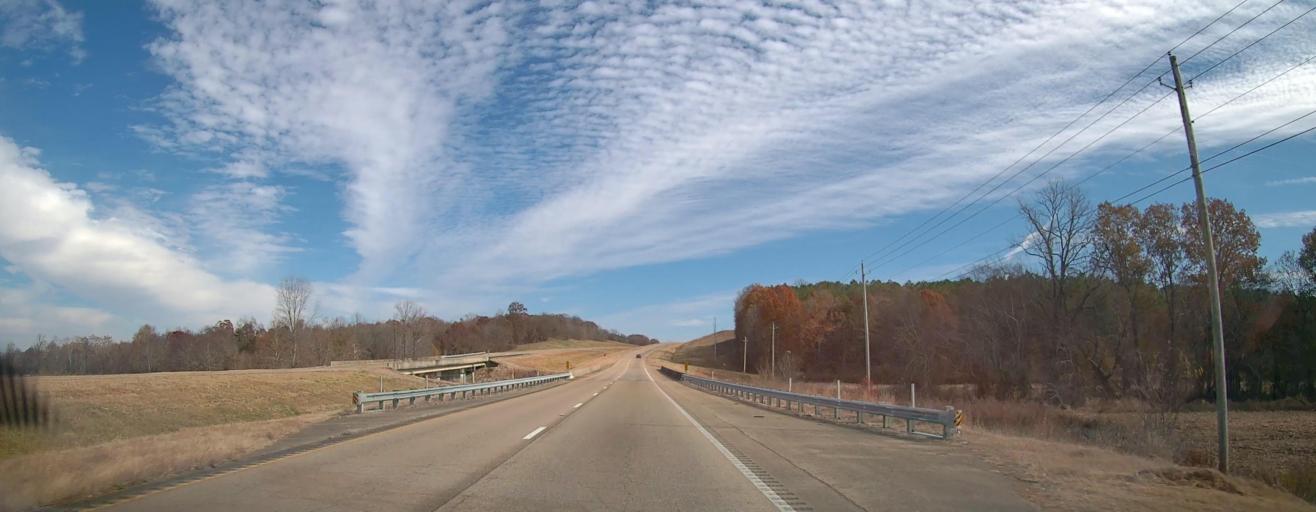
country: US
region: Mississippi
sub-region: Alcorn County
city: Corinth
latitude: 34.9322
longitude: -88.6537
